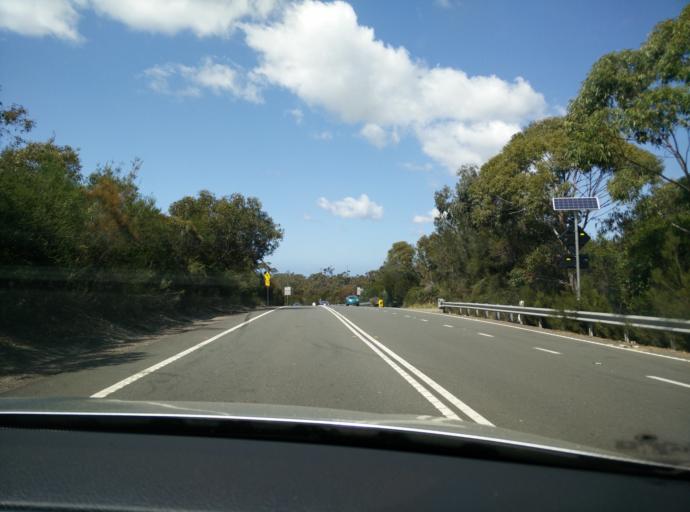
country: AU
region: New South Wales
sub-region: Gosford Shire
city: Blackwall
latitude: -33.4742
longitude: 151.2882
